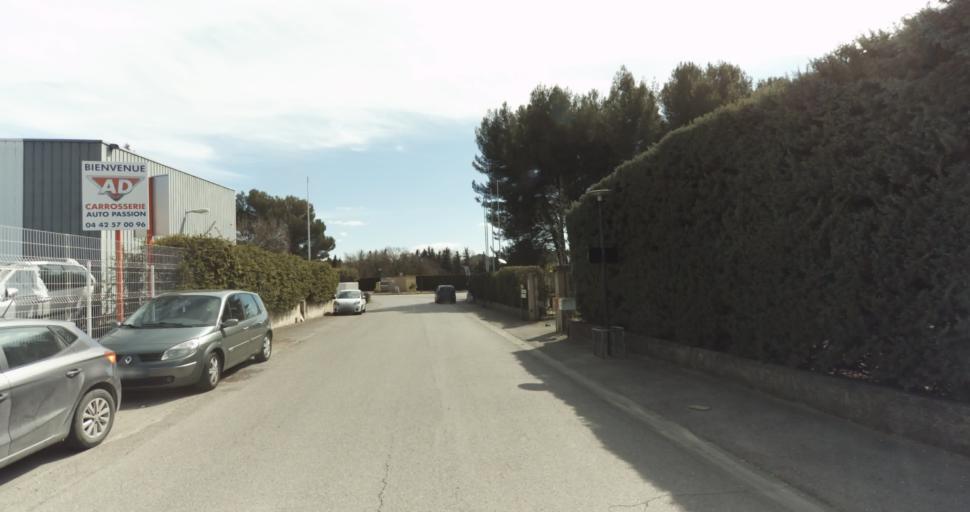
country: FR
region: Provence-Alpes-Cote d'Azur
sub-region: Departement des Bouches-du-Rhone
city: Saint-Cannat
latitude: 43.6122
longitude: 5.3223
